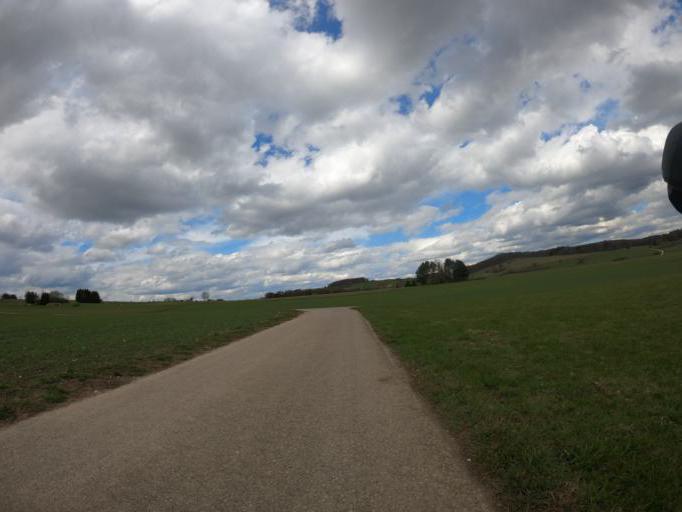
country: DE
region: Baden-Wuerttemberg
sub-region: Tuebingen Region
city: Pfullingen
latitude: 48.3902
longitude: 9.1955
